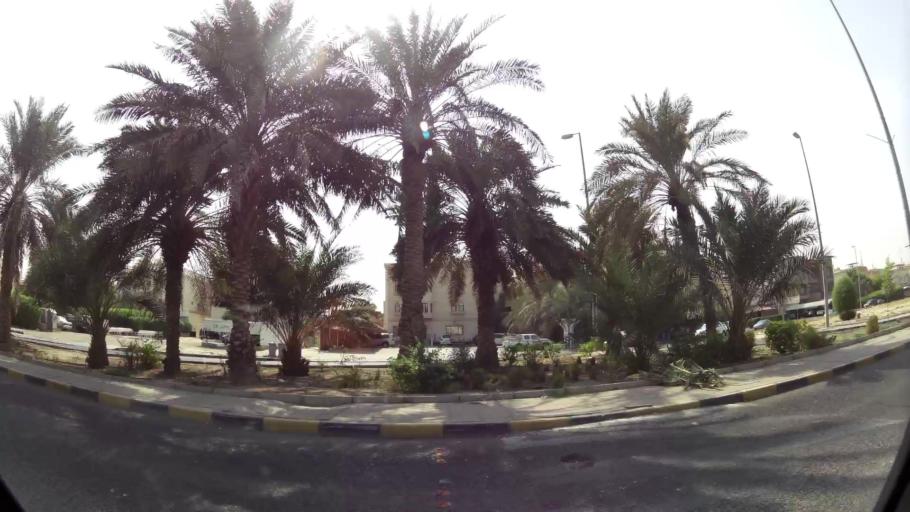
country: KW
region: Al Asimah
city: Ar Rabiyah
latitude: 29.3032
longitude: 47.8739
